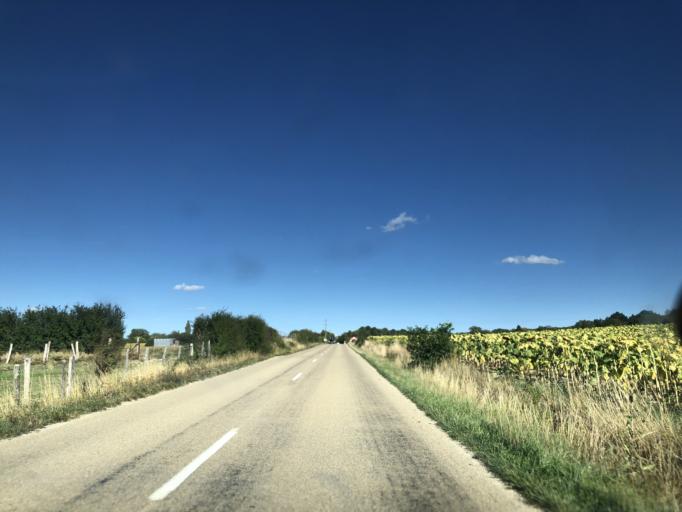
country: FR
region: Bourgogne
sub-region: Departement de l'Yonne
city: Seignelay
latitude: 47.9006
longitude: 3.5865
